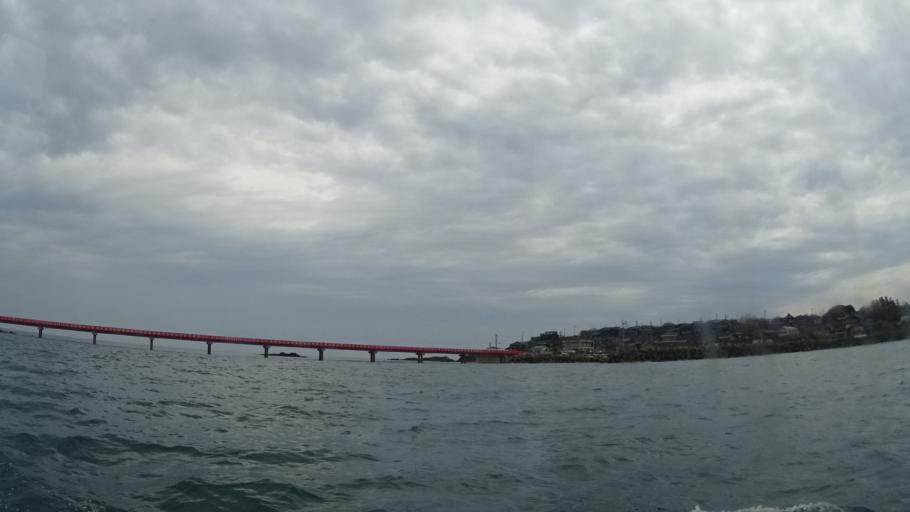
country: JP
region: Fukui
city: Mikuni
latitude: 36.2488
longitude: 136.1206
